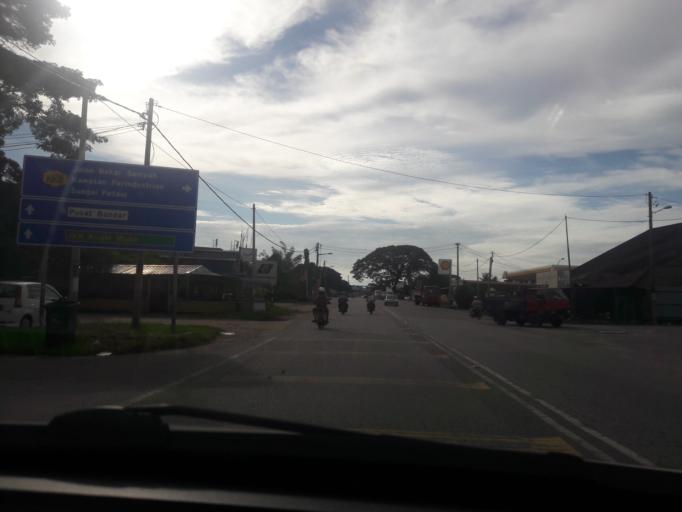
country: MY
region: Kedah
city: Sungai Petani
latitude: 5.6352
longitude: 100.5001
